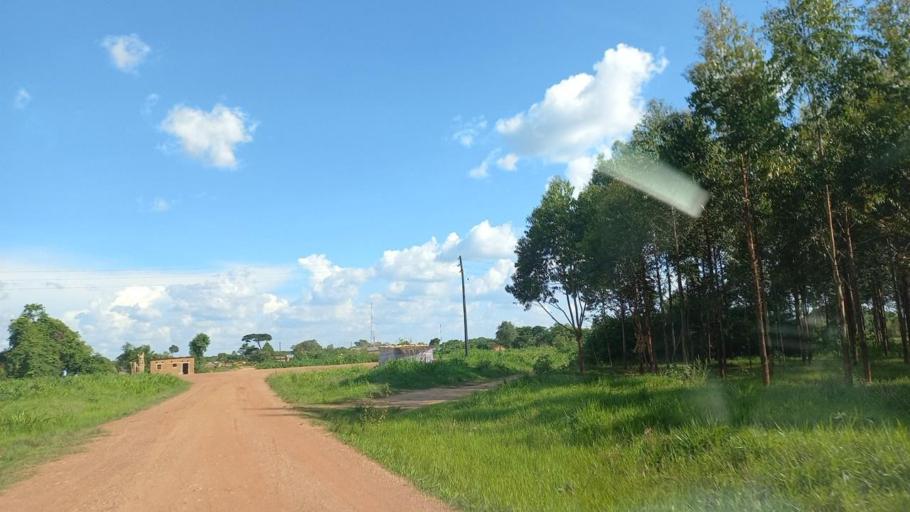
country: ZM
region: Copperbelt
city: Ndola
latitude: -12.8510
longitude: 28.5264
